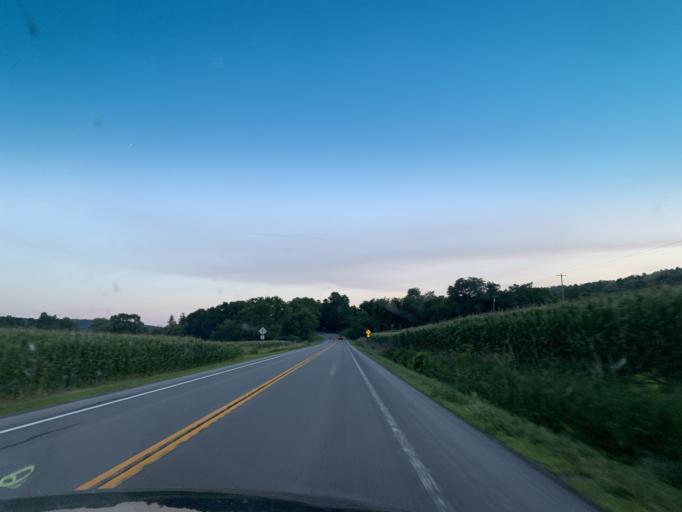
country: US
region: New York
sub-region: Chenango County
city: New Berlin
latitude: 42.7675
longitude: -75.2788
